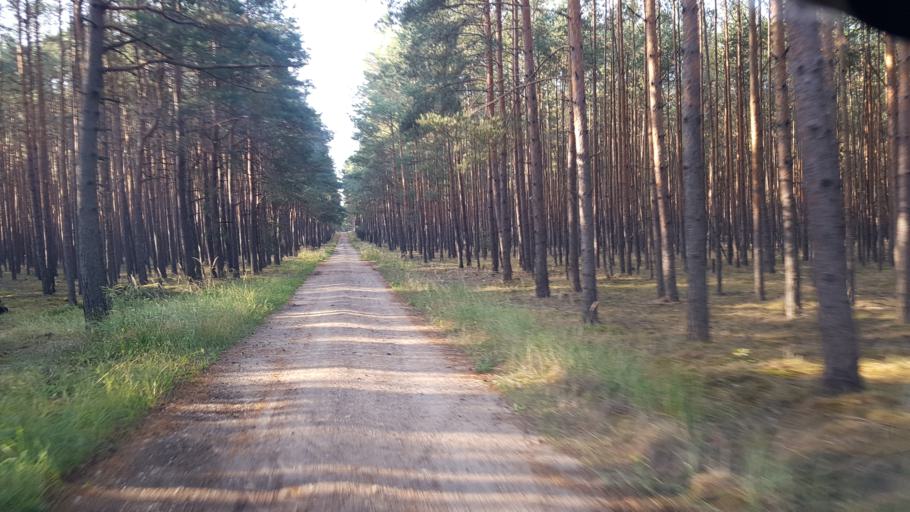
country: DE
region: Brandenburg
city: Sonnewalde
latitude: 51.6467
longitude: 13.6483
